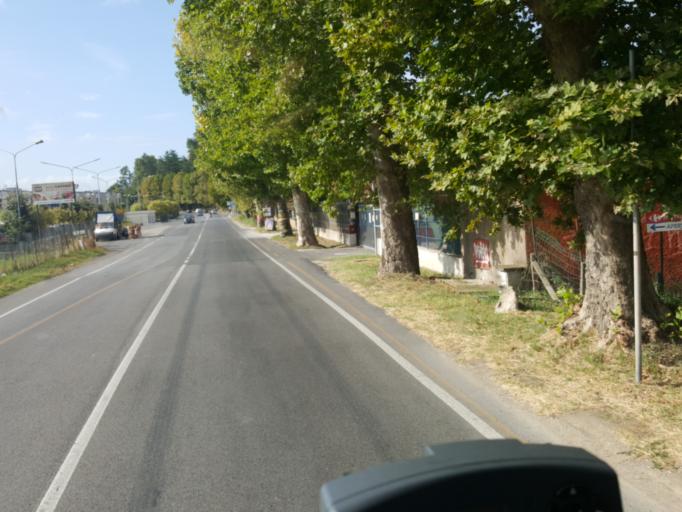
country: IT
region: Latium
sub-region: Citta metropolitana di Roma Capitale
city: Girardi-Bellavista-Terrazze
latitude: 42.1076
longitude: 12.5834
